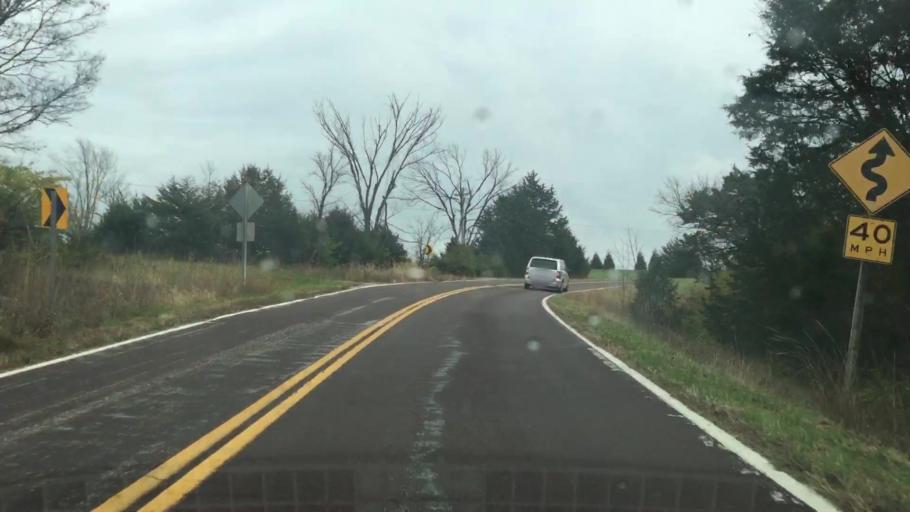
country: US
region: Missouri
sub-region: Callaway County
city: Fulton
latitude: 38.7785
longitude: -91.8460
